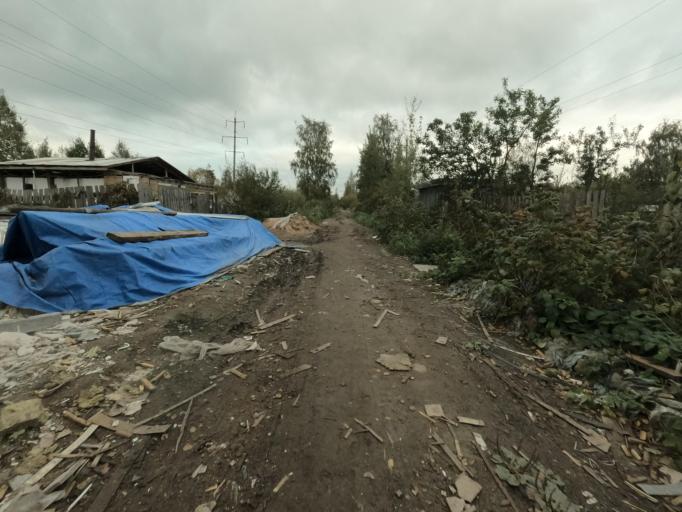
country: RU
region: St.-Petersburg
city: Sapernyy
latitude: 59.7770
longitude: 30.6429
